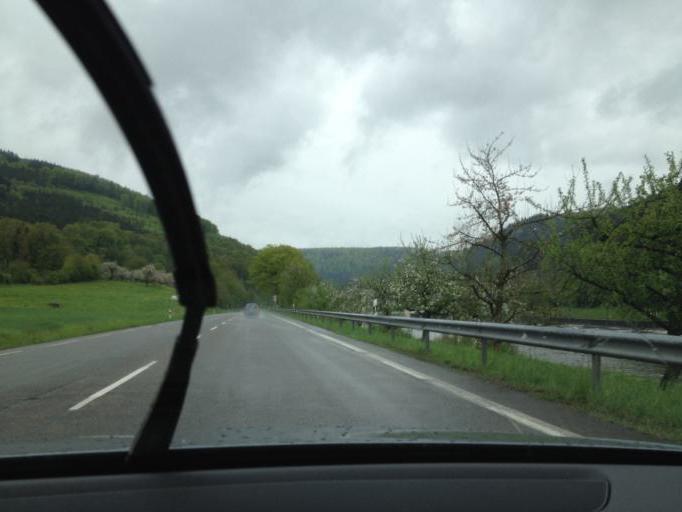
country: DE
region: Baden-Wuerttemberg
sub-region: Karlsruhe Region
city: Eberbach
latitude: 49.4370
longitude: 9.0066
